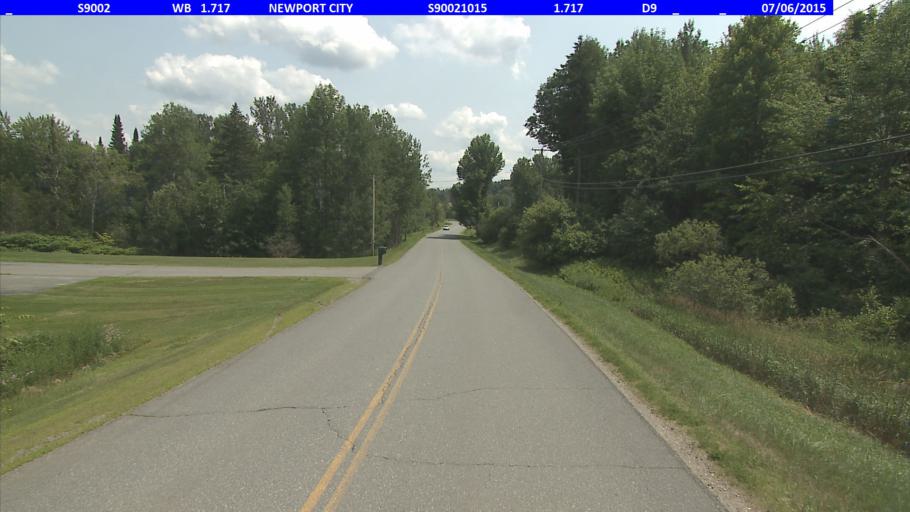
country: US
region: Vermont
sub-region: Orleans County
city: Newport
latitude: 44.9397
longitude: -72.2382
